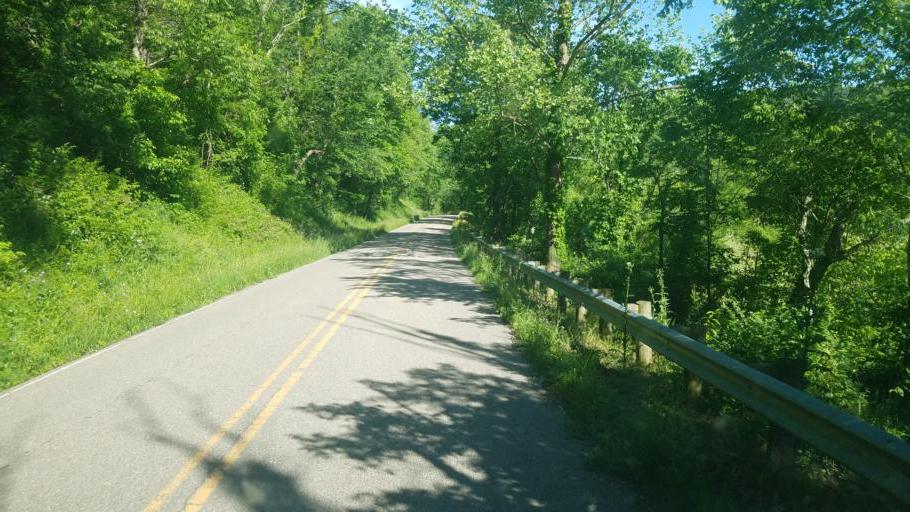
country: US
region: Ohio
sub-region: Tuscarawas County
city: Newcomerstown
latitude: 40.1797
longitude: -81.5602
